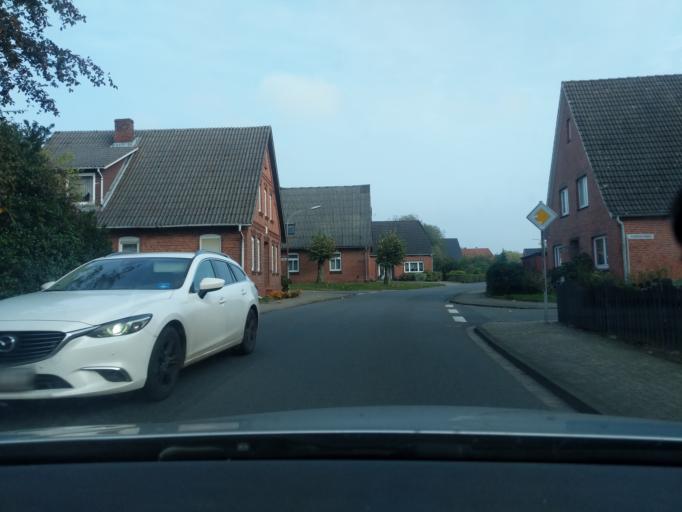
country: DE
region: Lower Saxony
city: Lamstedt
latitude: 53.6364
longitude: 9.0980
